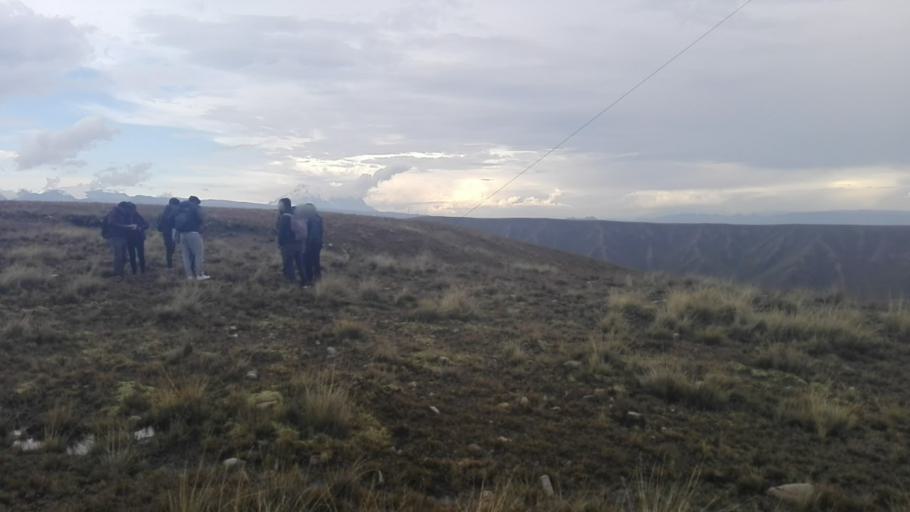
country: BO
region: La Paz
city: La Paz
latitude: -16.4111
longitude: -68.1180
